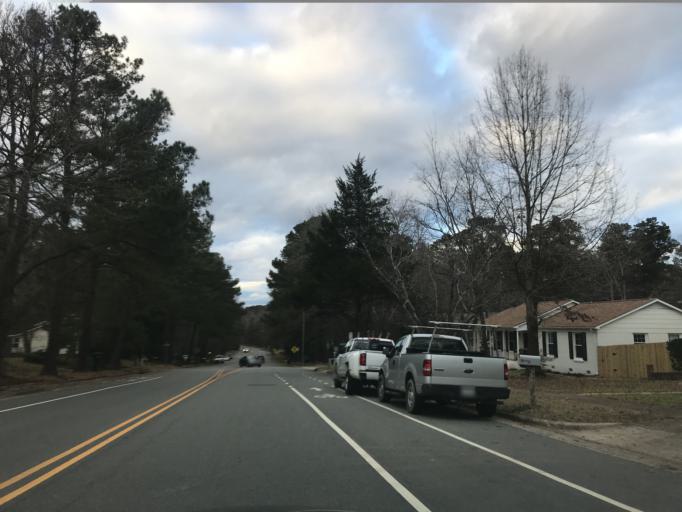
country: US
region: North Carolina
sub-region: Wake County
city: West Raleigh
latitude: 35.8623
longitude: -78.6538
